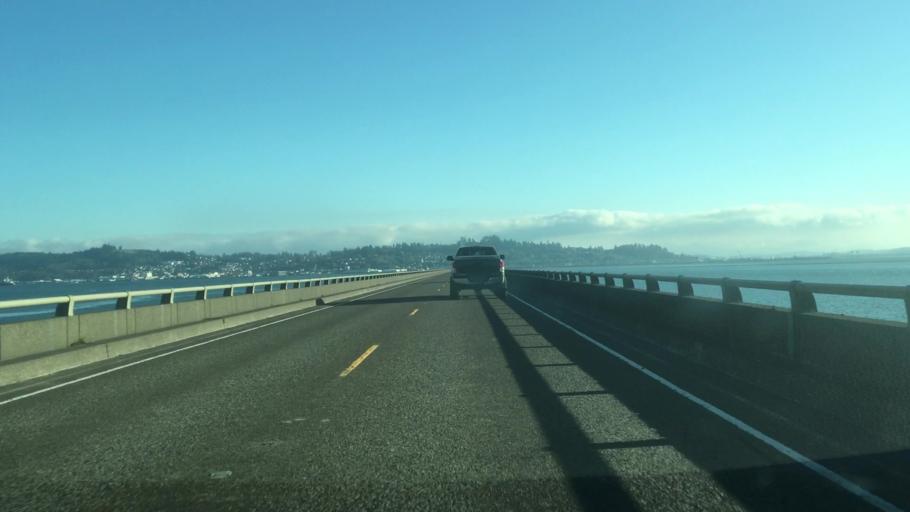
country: US
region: Oregon
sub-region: Clatsop County
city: Astoria
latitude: 46.2194
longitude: -123.8641
